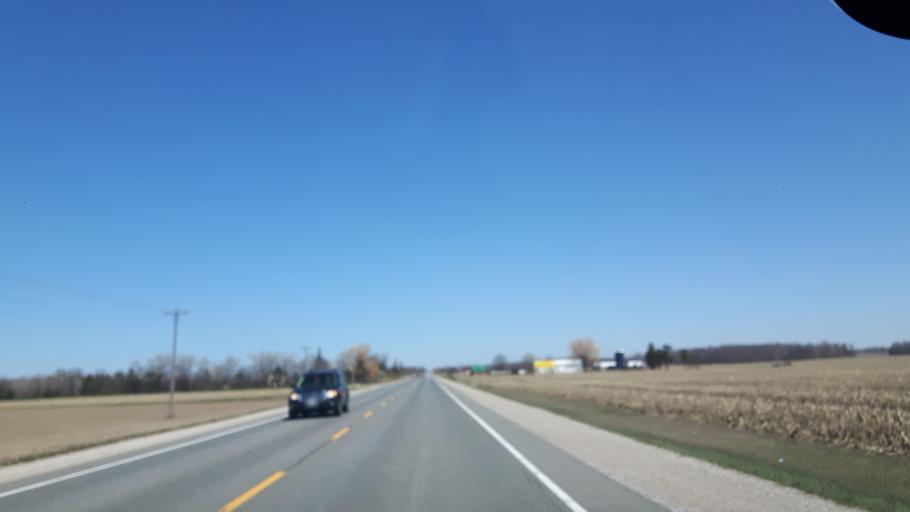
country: CA
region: Ontario
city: Goderich
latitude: 43.6283
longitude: -81.7056
